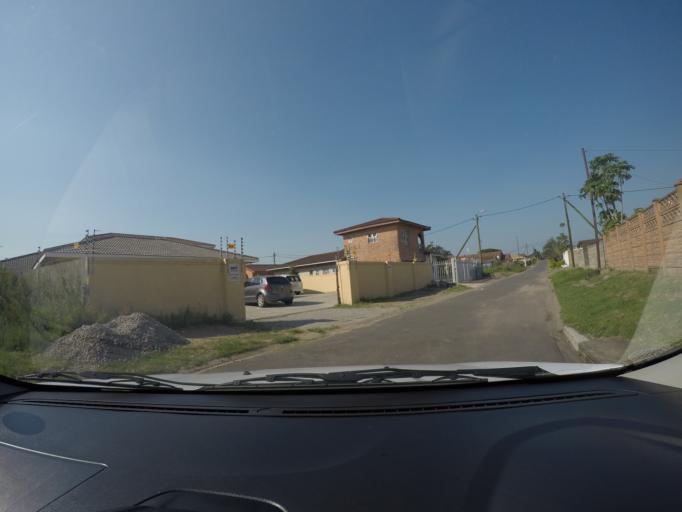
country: ZA
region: KwaZulu-Natal
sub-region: uThungulu District Municipality
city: Richards Bay
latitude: -28.7222
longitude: 32.0377
